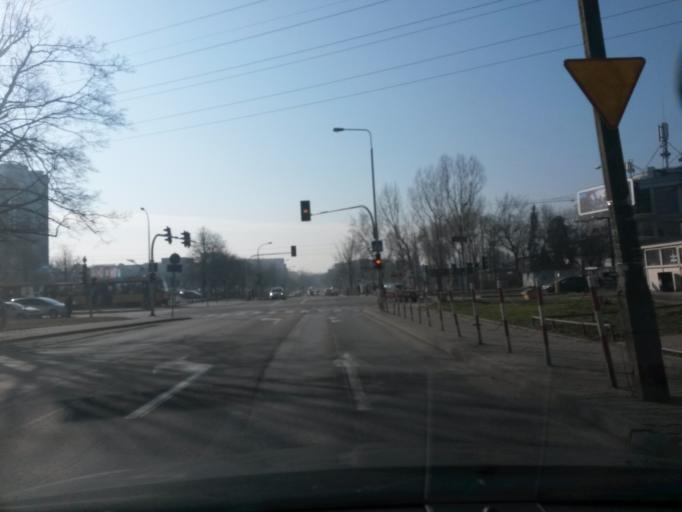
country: PL
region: Masovian Voivodeship
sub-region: Warszawa
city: Mokotow
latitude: 52.1895
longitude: 21.0074
